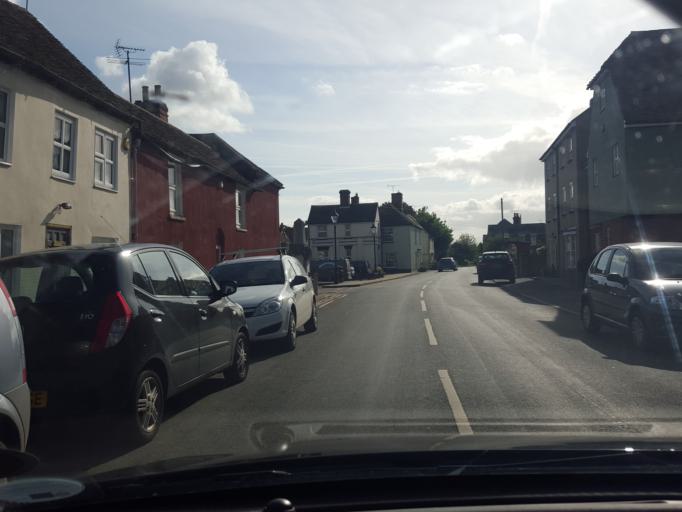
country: GB
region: England
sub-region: Essex
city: Little Clacton
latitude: 51.9040
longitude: 1.1889
